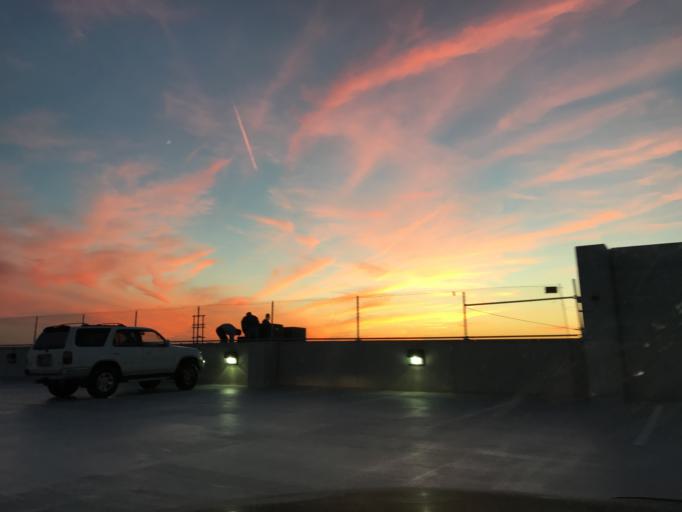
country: US
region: Maryland
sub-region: City of Baltimore
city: Baltimore
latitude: 39.3355
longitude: -76.6298
